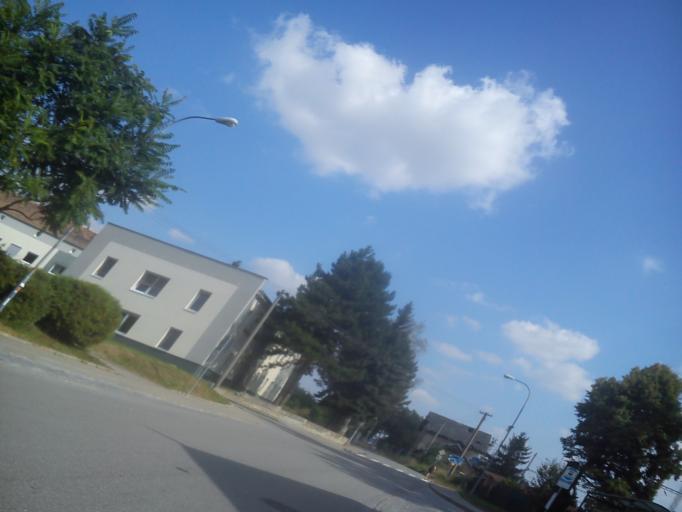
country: CZ
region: South Moravian
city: Sokolnice
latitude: 49.1084
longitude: 16.7338
